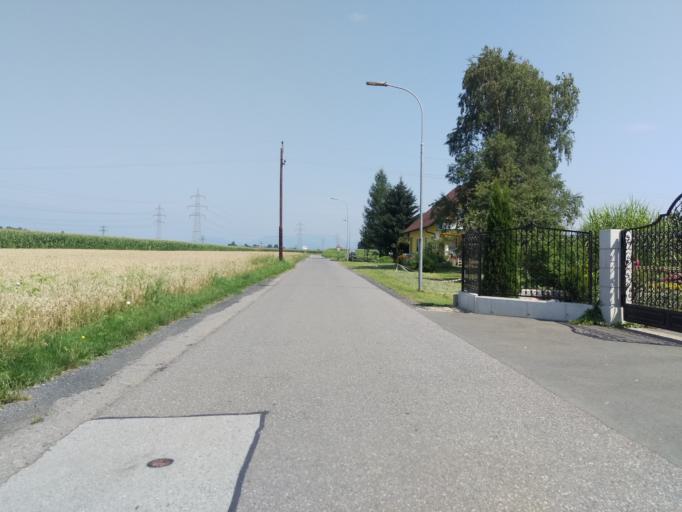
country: AT
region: Styria
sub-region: Politischer Bezirk Graz-Umgebung
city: Werndorf
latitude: 46.9270
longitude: 15.4901
